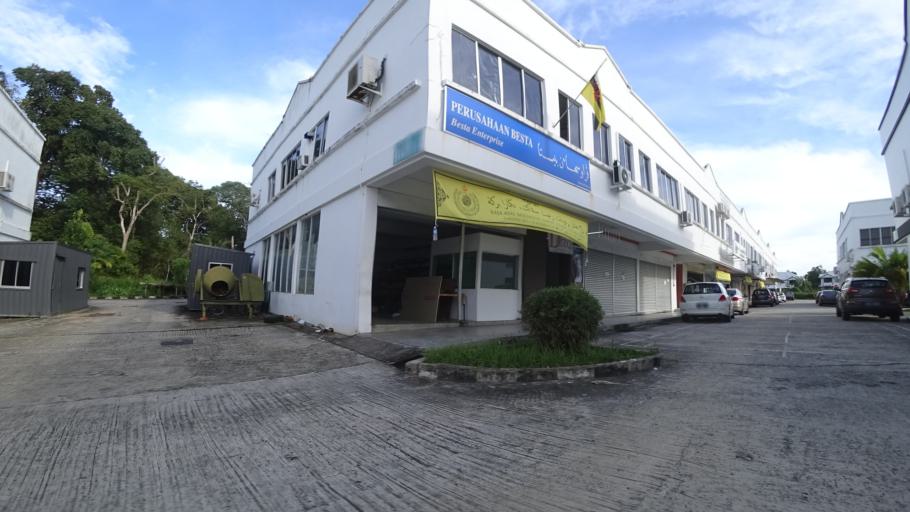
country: BN
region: Brunei and Muara
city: Bandar Seri Begawan
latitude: 4.8935
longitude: 114.8380
